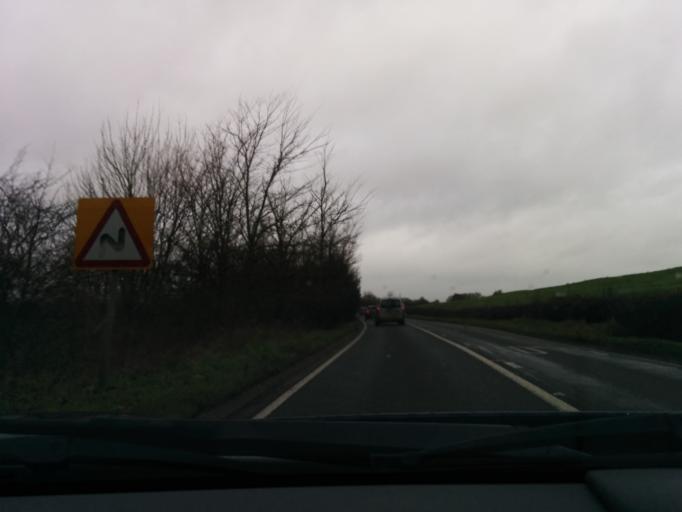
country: GB
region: England
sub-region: Oxfordshire
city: Eynsham
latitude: 51.7674
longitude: -1.3577
